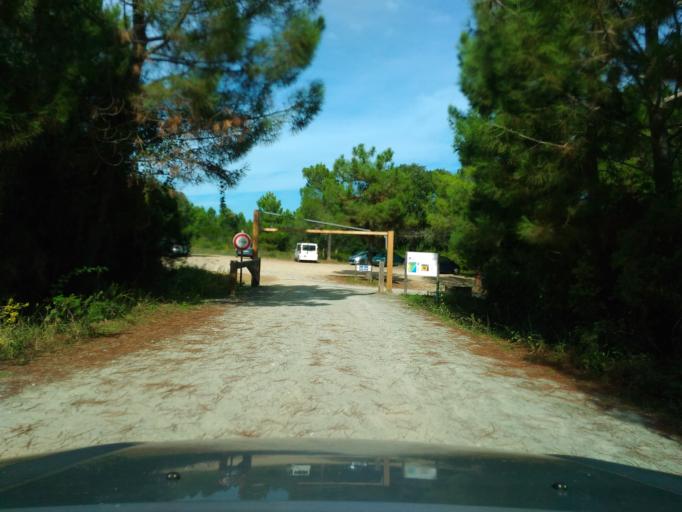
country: FR
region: Corsica
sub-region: Departement de la Haute-Corse
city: Ghisonaccia
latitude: 42.0125
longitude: 9.4592
